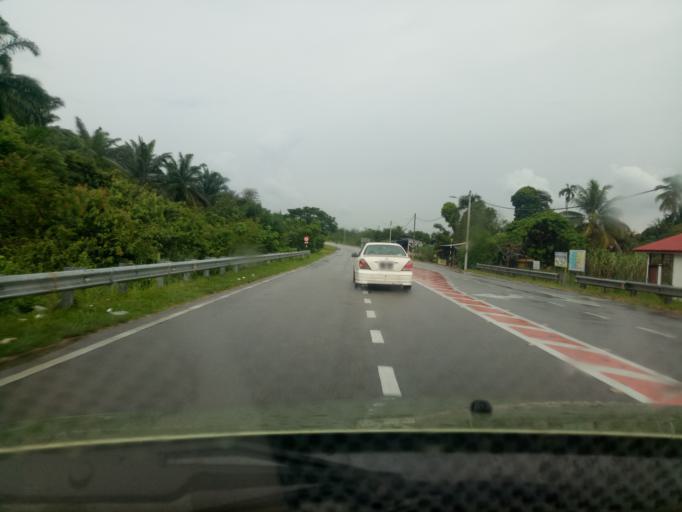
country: MY
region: Penang
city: Tasek Glugor
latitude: 5.5201
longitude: 100.5782
